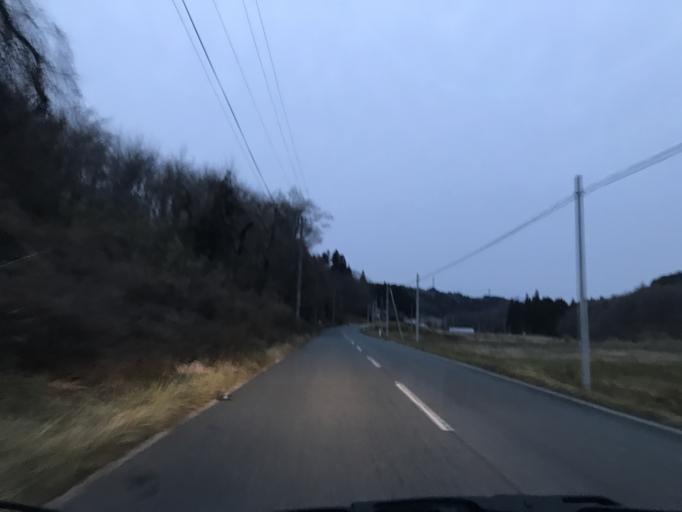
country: JP
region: Iwate
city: Ichinoseki
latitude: 38.8284
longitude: 141.1187
